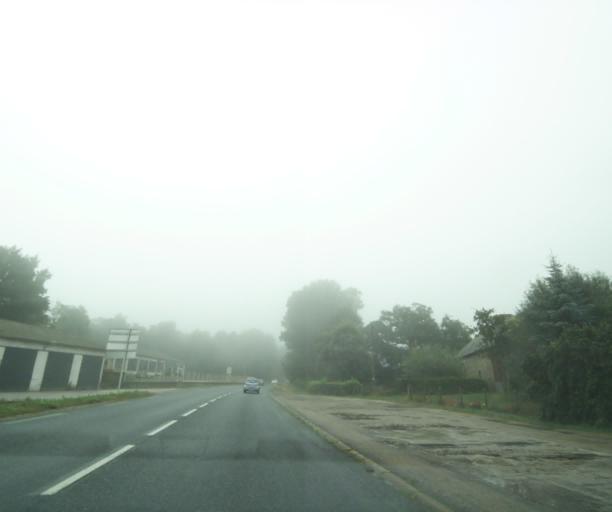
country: FR
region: Midi-Pyrenees
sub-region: Departement de l'Aveyron
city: Baraqueville
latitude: 44.2709
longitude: 2.4216
